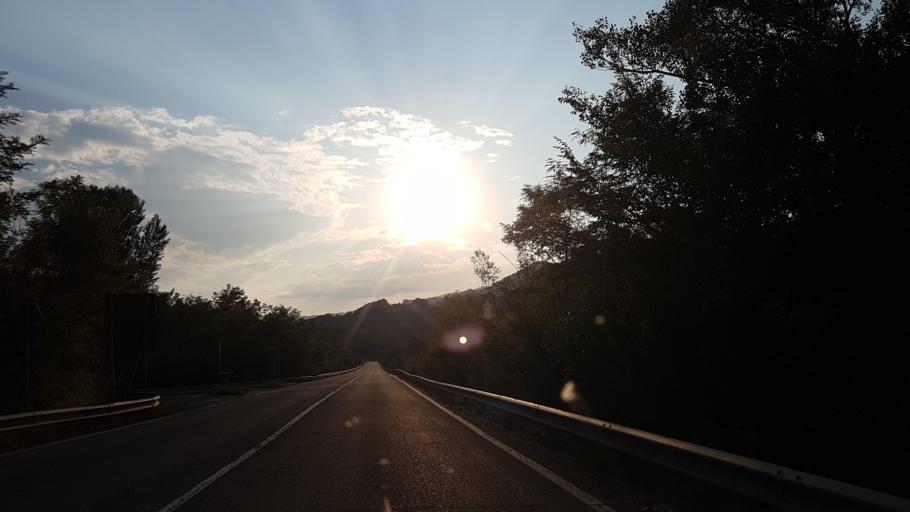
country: IT
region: Emilia-Romagna
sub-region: Provincia di Parma
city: Stazione Valmozzola
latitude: 44.5485
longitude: 9.9144
